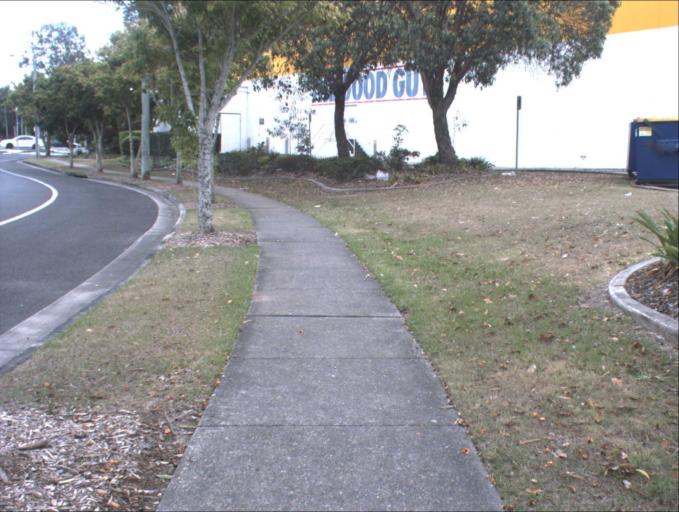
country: AU
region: Queensland
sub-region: Logan
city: Slacks Creek
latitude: -27.6567
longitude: 153.1677
